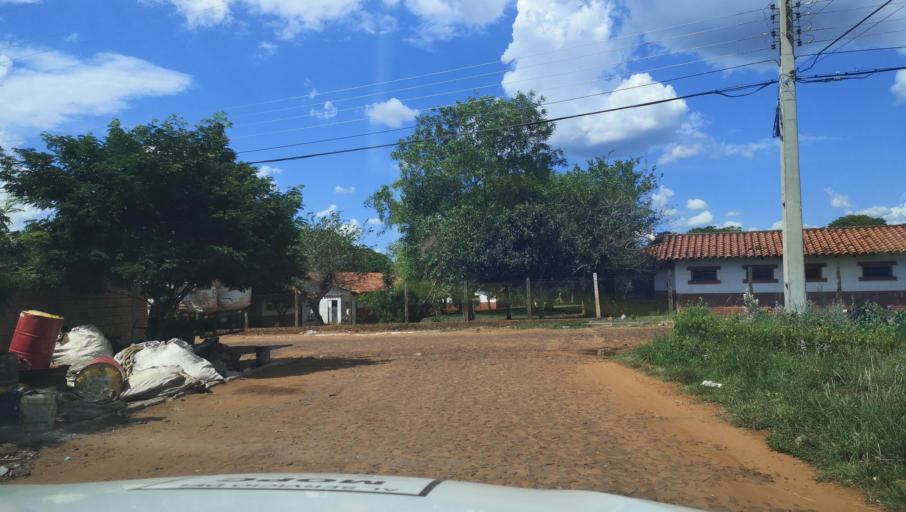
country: PY
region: Misiones
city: Santa Maria
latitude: -26.8920
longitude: -57.0351
